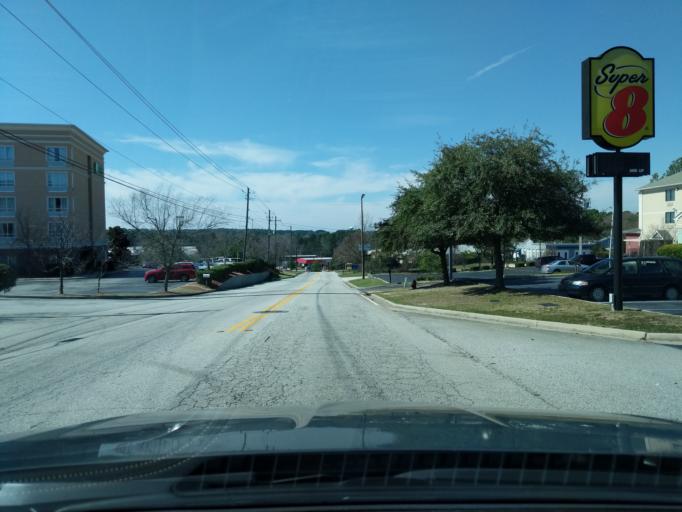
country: US
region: Georgia
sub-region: Columbia County
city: Evans
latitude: 33.4801
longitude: -82.1332
